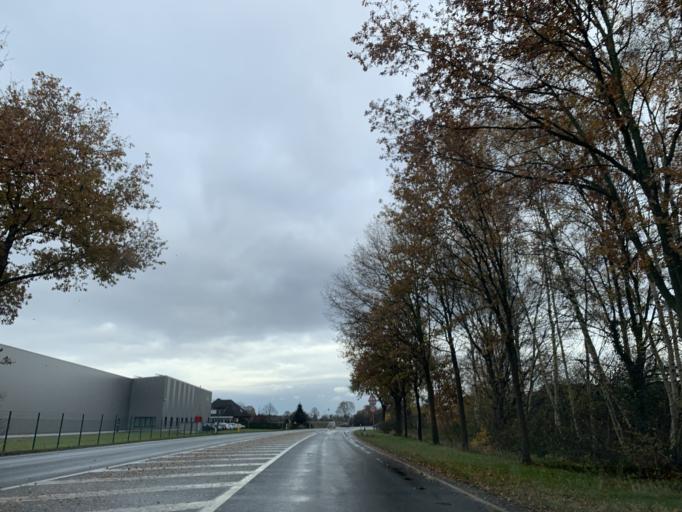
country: NL
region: Overijssel
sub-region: Gemeente Enschede
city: Enschede
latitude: 52.1363
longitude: 6.9138
